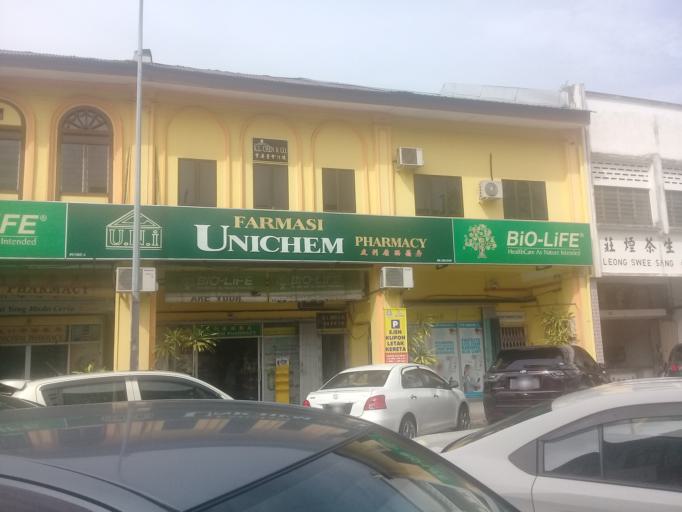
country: MY
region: Perak
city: Ipoh
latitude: 4.5957
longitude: 101.0784
